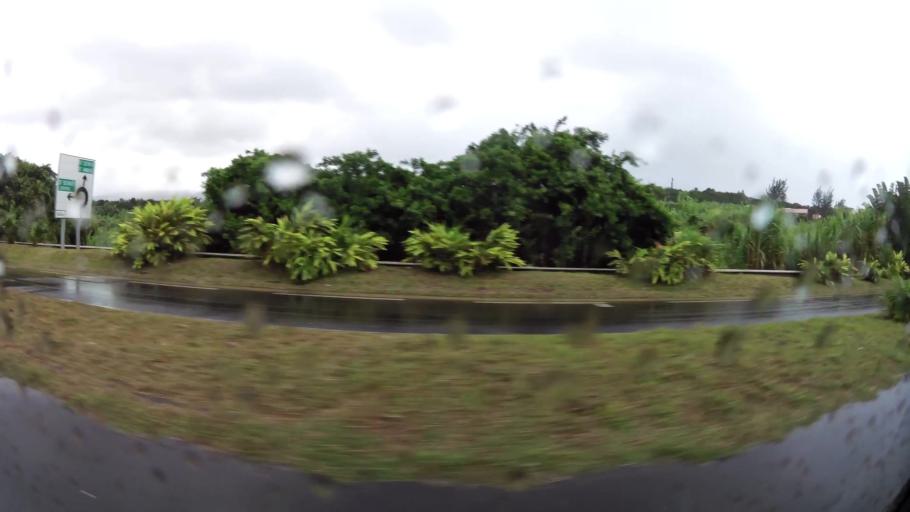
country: RE
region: Reunion
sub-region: Reunion
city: Saint-Benoit
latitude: -21.0249
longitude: 55.7045
